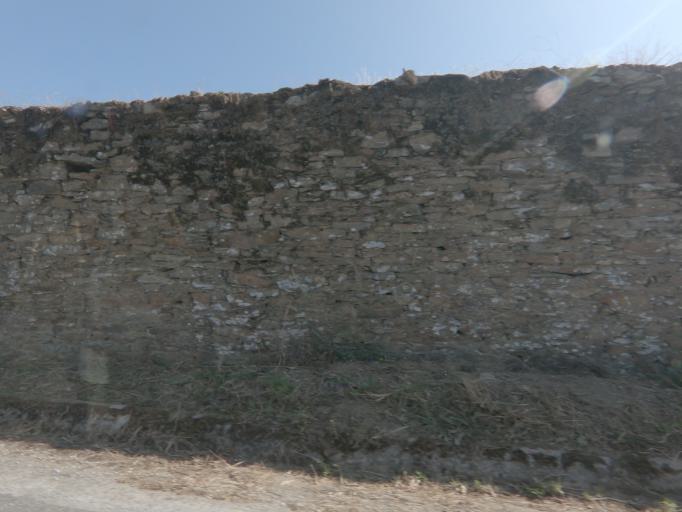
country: PT
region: Vila Real
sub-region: Sabrosa
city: Vilela
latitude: 41.2344
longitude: -7.5720
